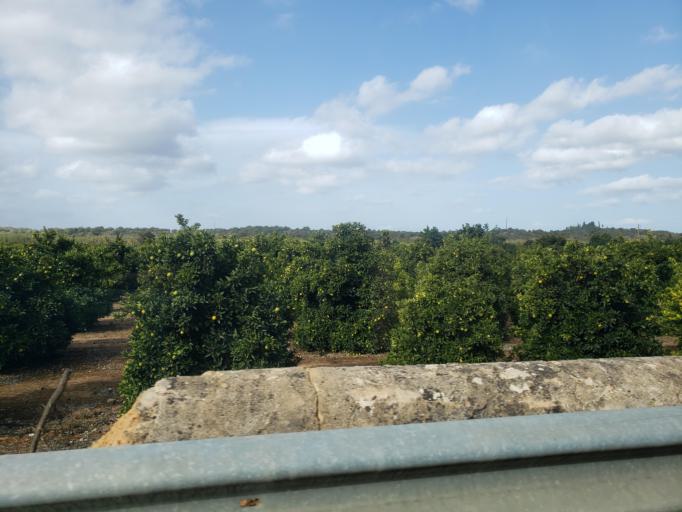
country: PT
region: Faro
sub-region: Portimao
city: Alvor
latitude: 37.1709
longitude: -8.5793
